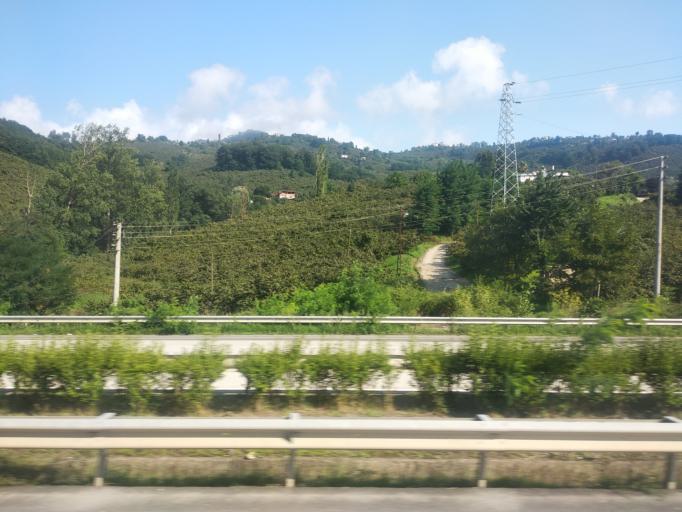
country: TR
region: Ordu
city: Ordu
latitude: 41.0090
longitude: 37.8307
